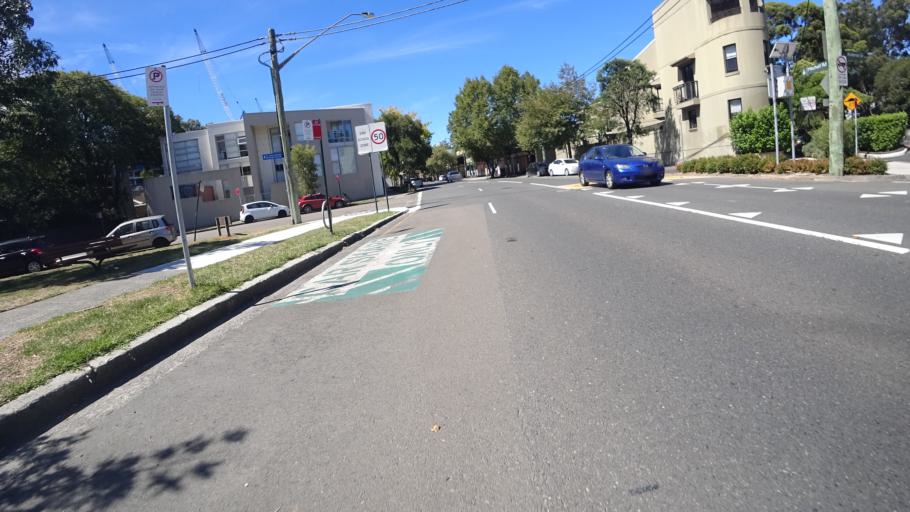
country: AU
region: New South Wales
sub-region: City of Sydney
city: Alexandria
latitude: -33.8992
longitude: 151.1946
